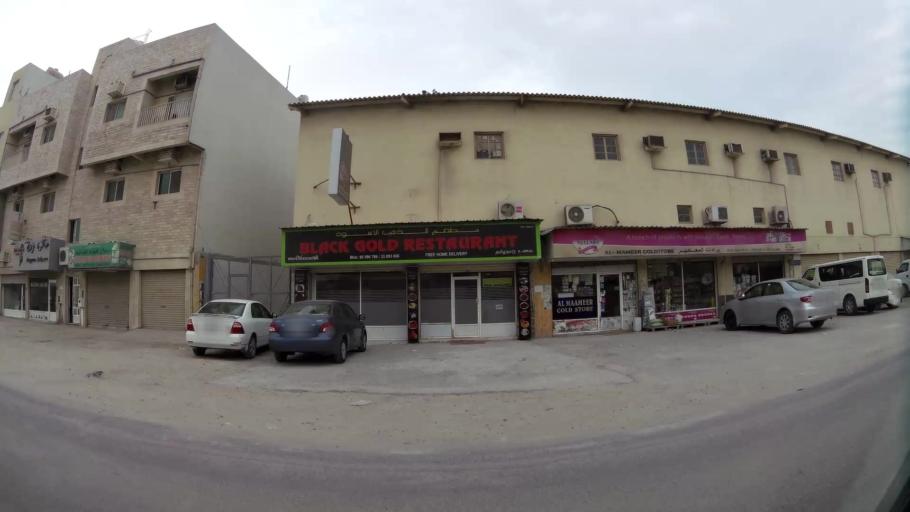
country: BH
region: Northern
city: Sitrah
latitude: 26.1406
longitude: 50.6042
